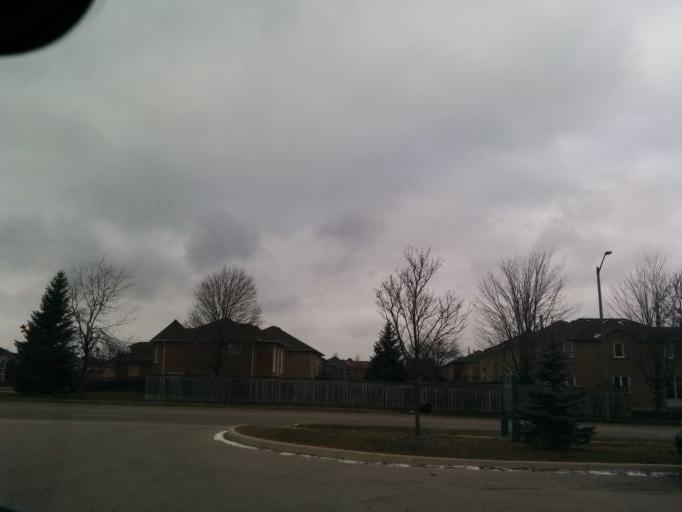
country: CA
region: Ontario
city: Brampton
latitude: 43.7438
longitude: -79.8337
